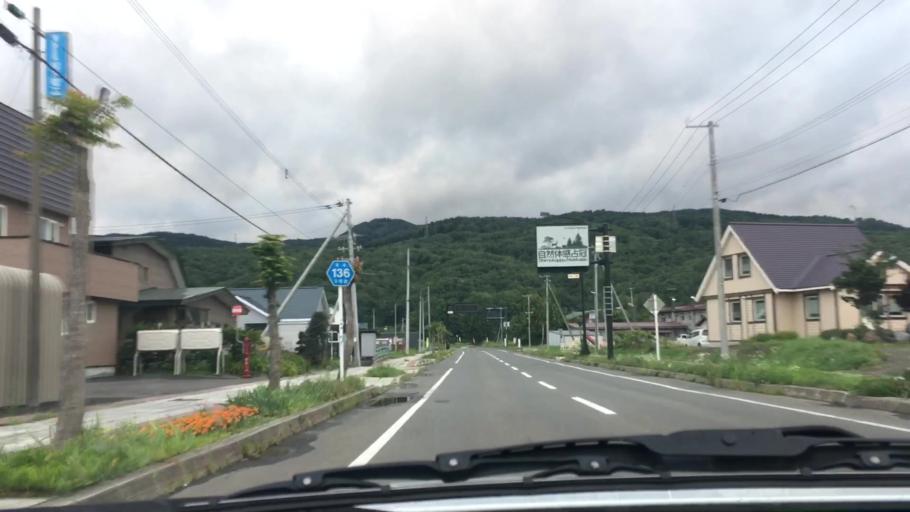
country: JP
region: Hokkaido
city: Shimo-furano
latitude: 42.9795
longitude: 142.3970
